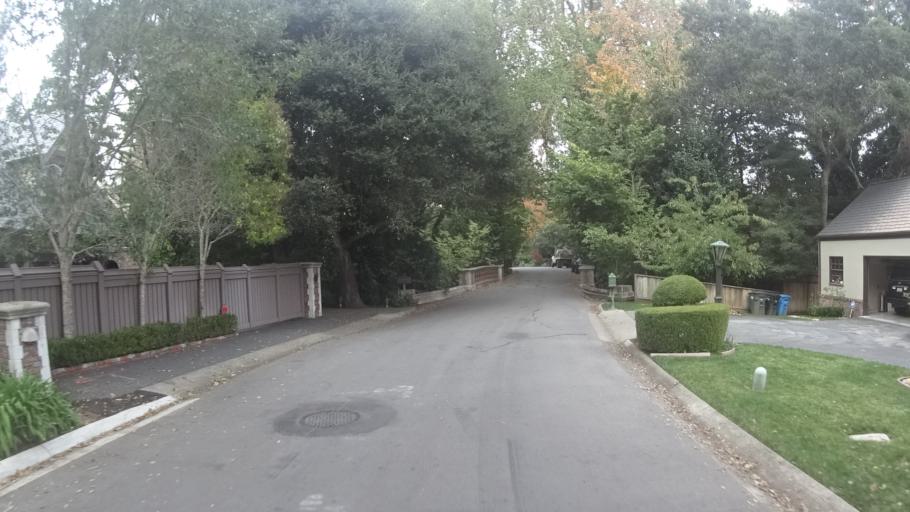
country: US
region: California
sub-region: San Mateo County
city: Hillsborough
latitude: 37.5736
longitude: -122.3696
